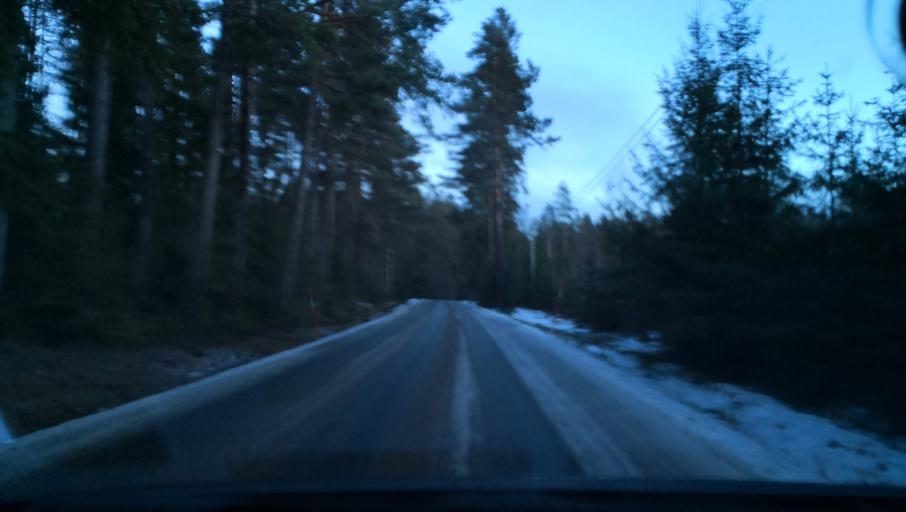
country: SE
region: Soedermanland
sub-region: Katrineholms Kommun
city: Katrineholm
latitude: 59.0805
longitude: 16.2399
